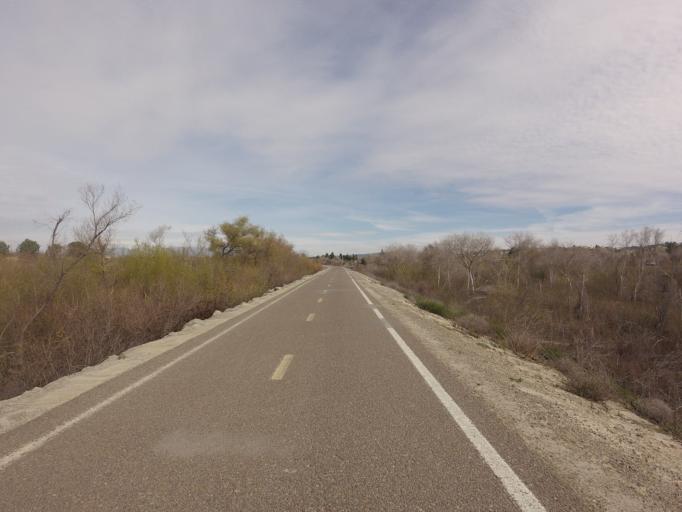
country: US
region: California
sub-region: San Diego County
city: Camp Pendleton South
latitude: 33.2399
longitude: -117.3109
